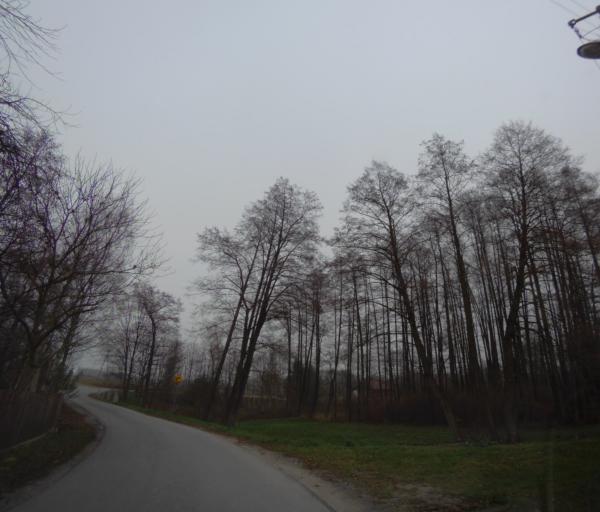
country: PL
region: Subcarpathian Voivodeship
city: Nowa Sarzyna
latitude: 50.2873
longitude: 22.3562
